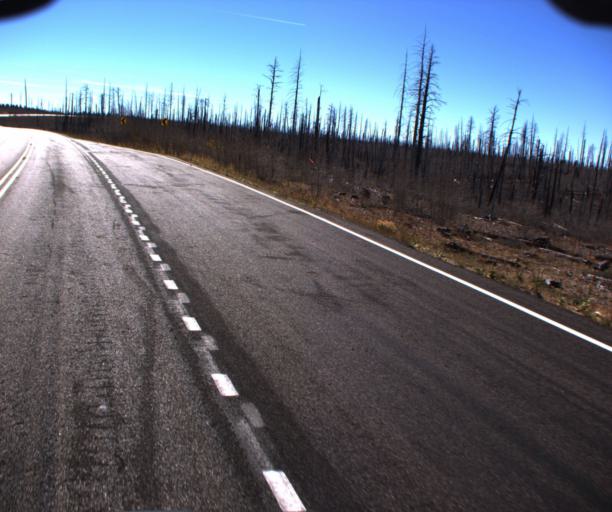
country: US
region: Arizona
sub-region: Coconino County
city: Grand Canyon
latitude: 36.5670
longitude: -112.1727
